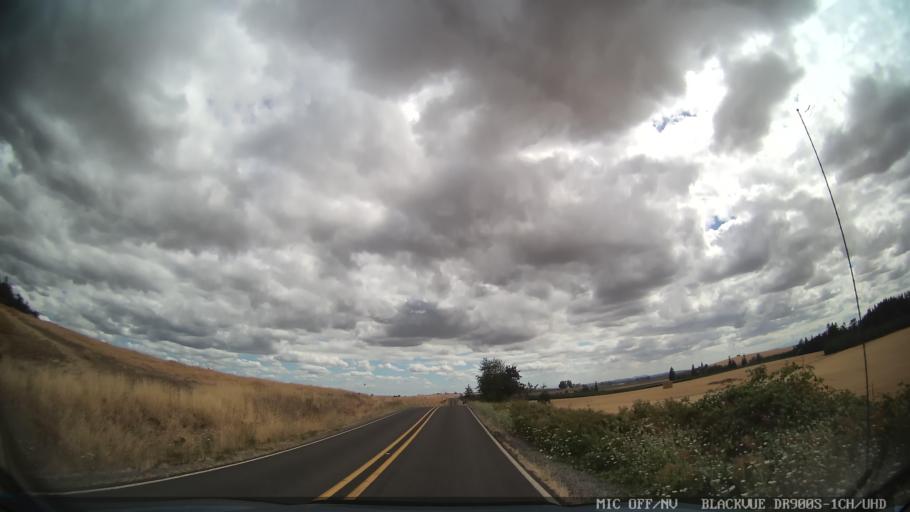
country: US
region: Oregon
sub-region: Marion County
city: Sublimity
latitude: 44.8630
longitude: -122.7386
